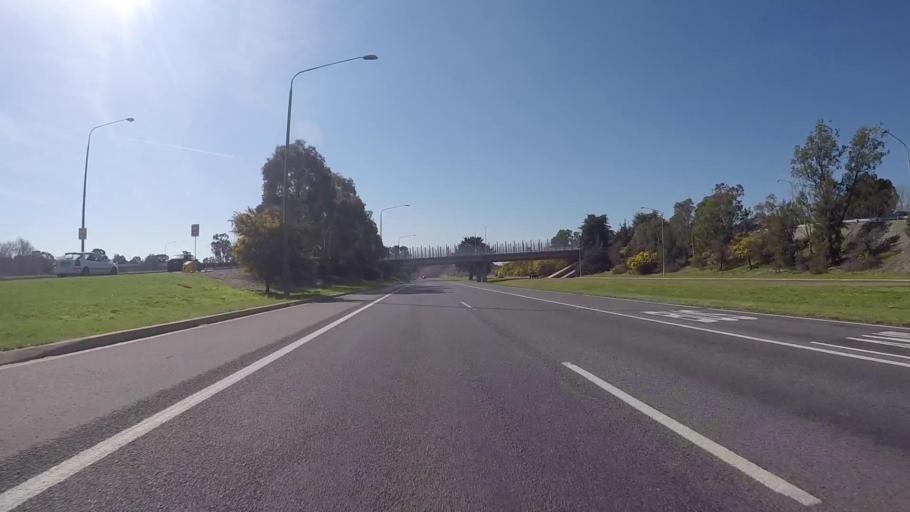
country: AU
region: Australian Capital Territory
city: Forrest
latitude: -35.3275
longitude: 149.0866
